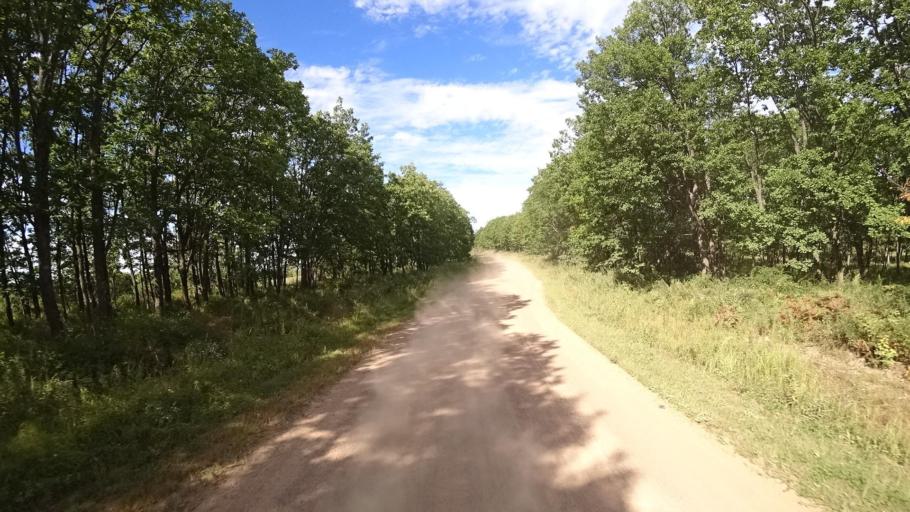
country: RU
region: Primorskiy
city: Yakovlevka
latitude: 44.4112
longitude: 133.5693
